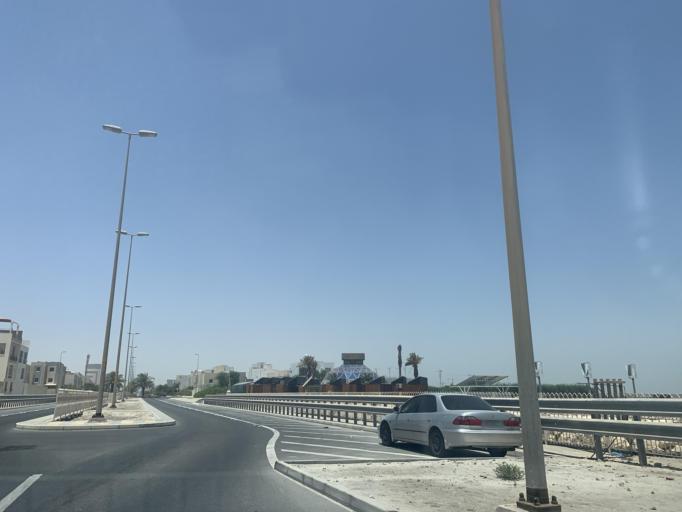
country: BH
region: Manama
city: Jidd Hafs
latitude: 26.2391
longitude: 50.4715
